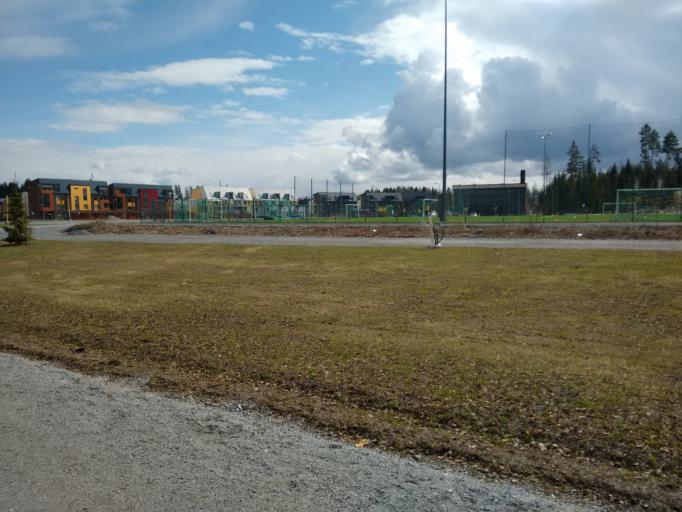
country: FI
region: Pirkanmaa
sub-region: Tampere
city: Tampere
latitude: 61.4388
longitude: 23.8089
